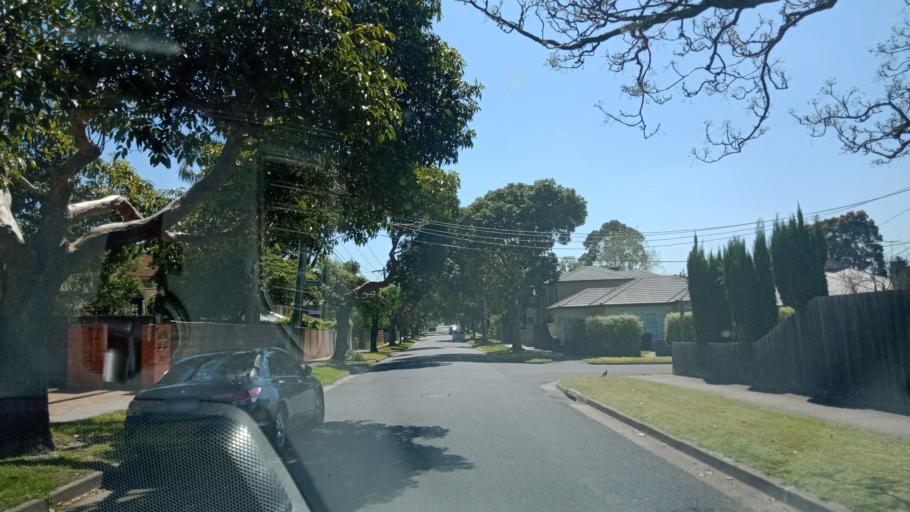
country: AU
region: Victoria
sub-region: Monash
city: Oakleigh South
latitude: -37.9304
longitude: 145.0782
